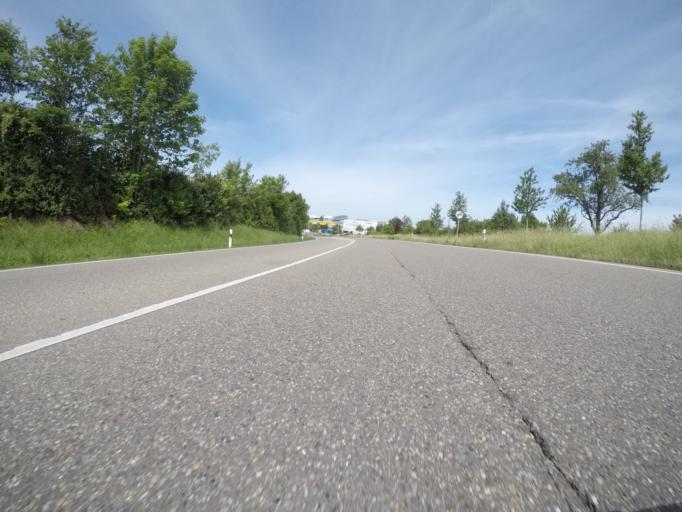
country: DE
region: Baden-Wuerttemberg
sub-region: Regierungsbezirk Stuttgart
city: Korntal
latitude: 48.8169
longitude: 9.1006
